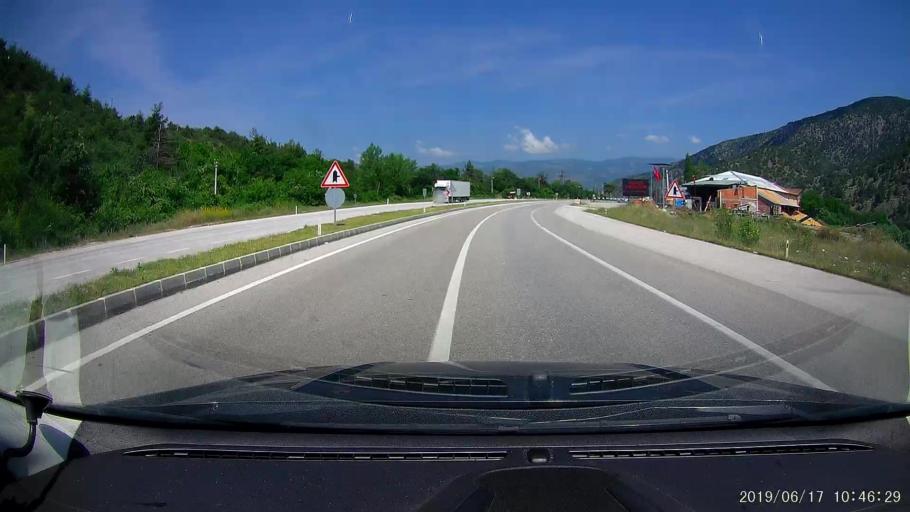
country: TR
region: Corum
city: Hacihamza
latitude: 41.0682
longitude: 34.4608
